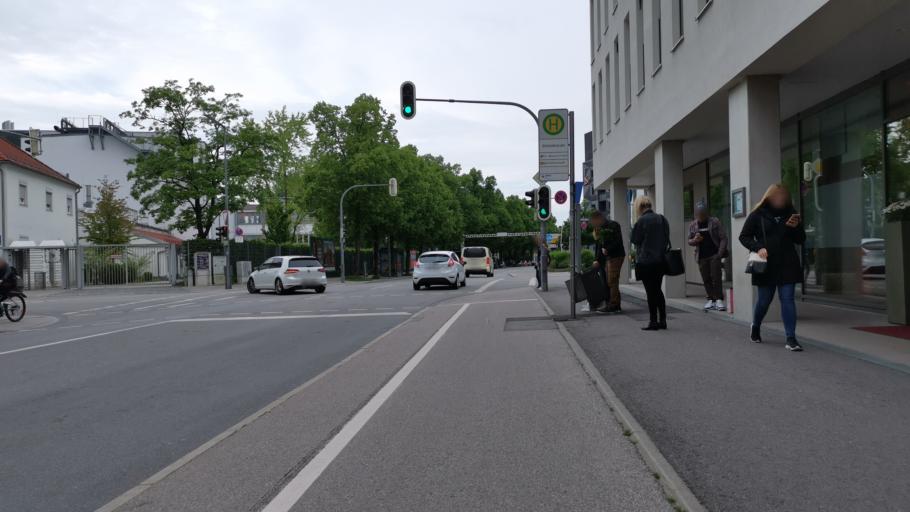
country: DE
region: Bavaria
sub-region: Upper Bavaria
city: Pullach im Isartal
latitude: 48.1023
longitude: 11.5300
